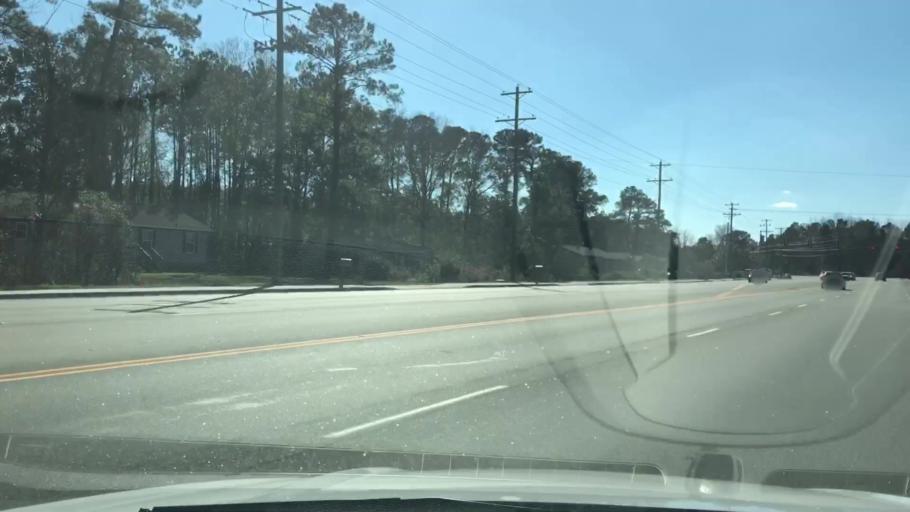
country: US
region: South Carolina
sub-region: Horry County
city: Garden City
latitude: 33.6402
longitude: -79.0309
